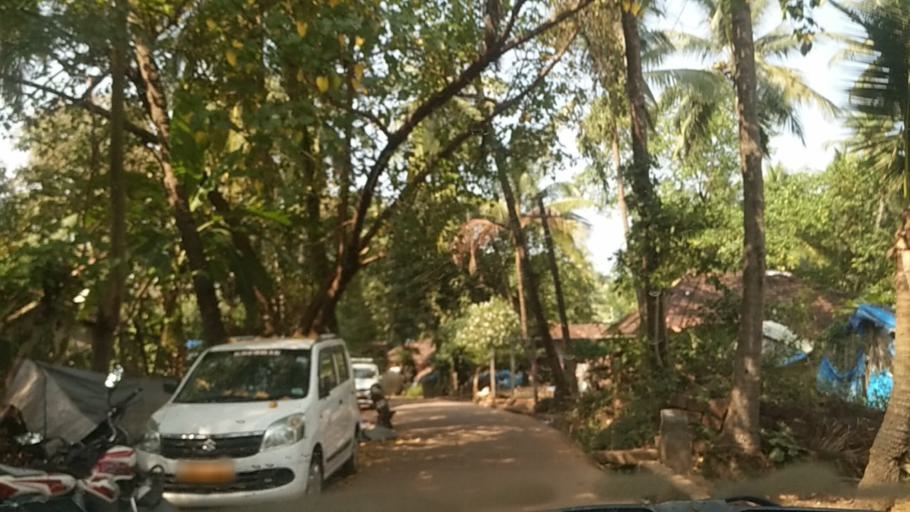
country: IN
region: Goa
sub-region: South Goa
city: Kankon
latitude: 15.0144
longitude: 74.0200
